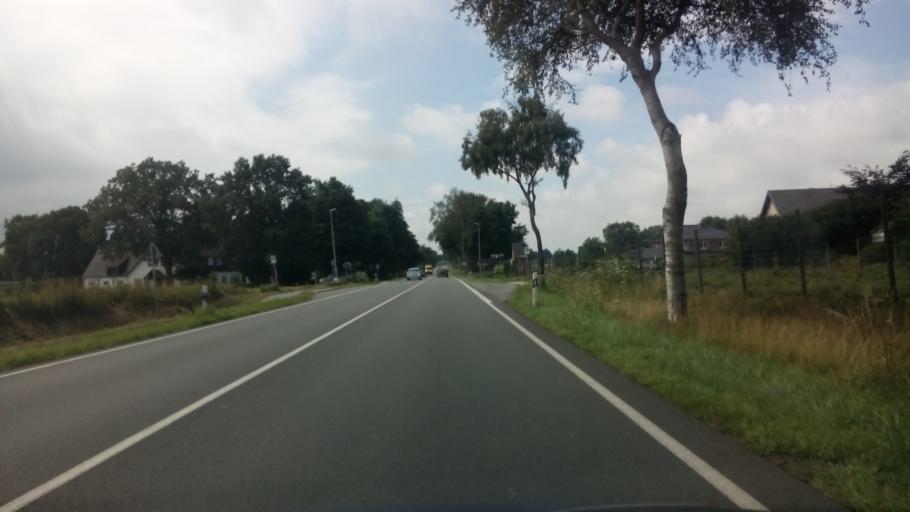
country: DE
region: Lower Saxony
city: Twistringen
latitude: 52.8113
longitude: 8.6609
